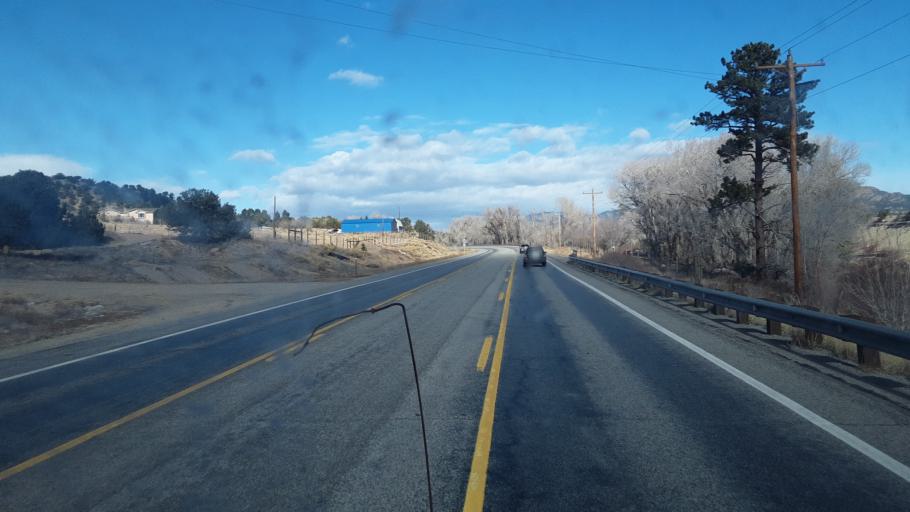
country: US
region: Colorado
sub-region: Chaffee County
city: Buena Vista
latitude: 38.7752
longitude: -106.1062
